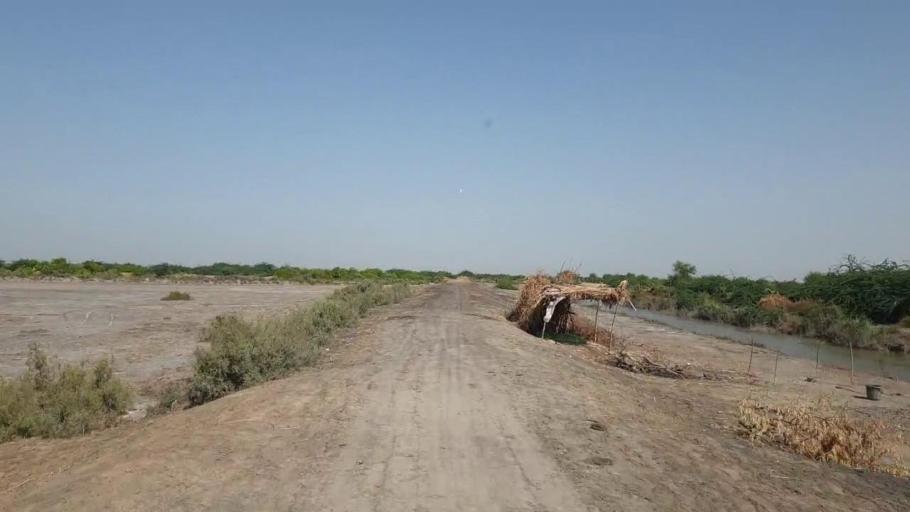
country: PK
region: Sindh
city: Tando Bago
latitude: 24.7072
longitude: 69.0713
